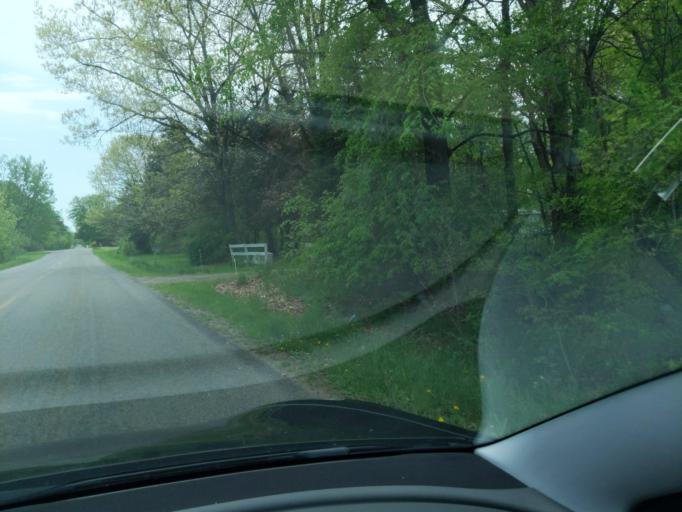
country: US
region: Michigan
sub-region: Ingham County
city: Stockbridge
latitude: 42.4650
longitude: -84.2247
